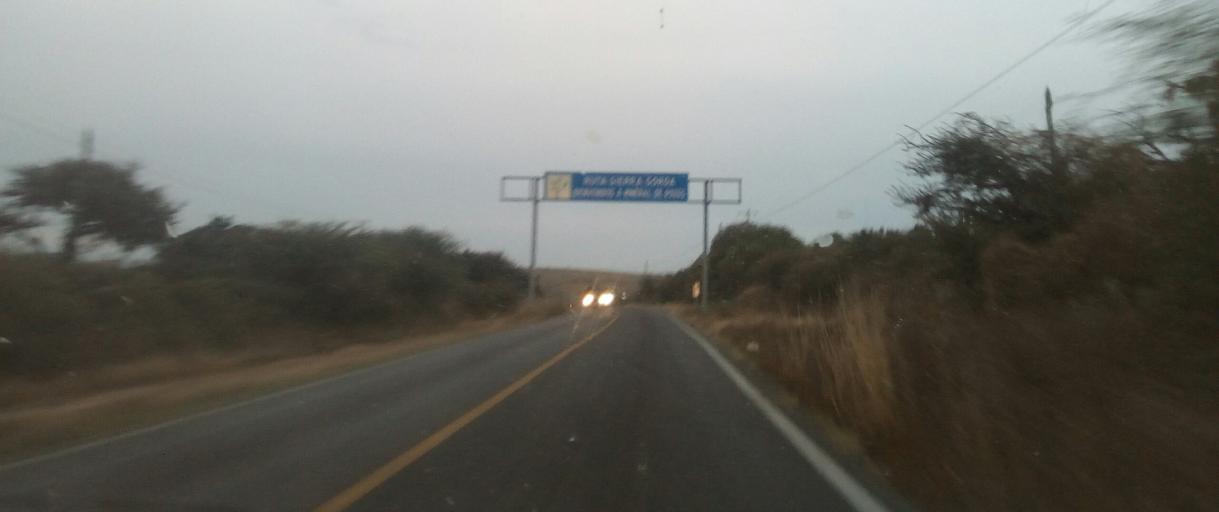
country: MX
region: Guanajuato
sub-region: San Luis de la Paz
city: San Ignacio
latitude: 21.2358
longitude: -100.4908
